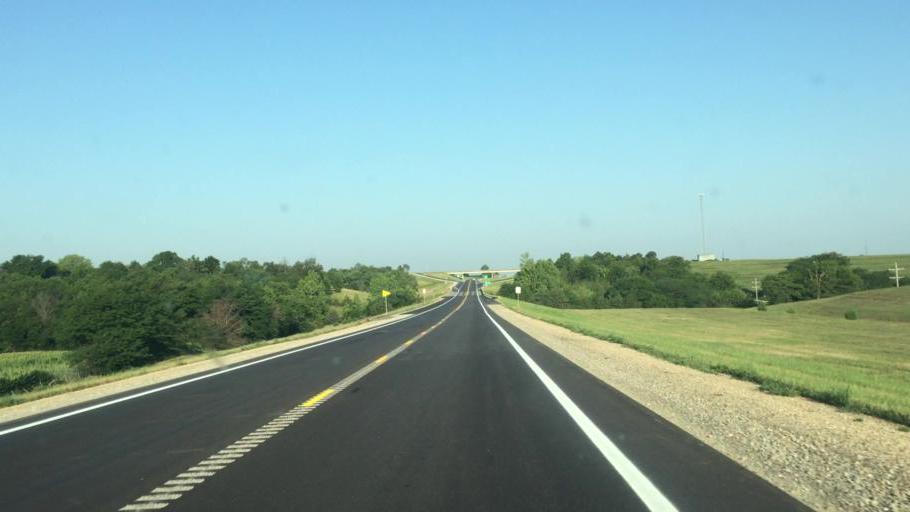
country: US
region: Kansas
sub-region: Brown County
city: Hiawatha
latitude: 39.8407
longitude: -95.4797
